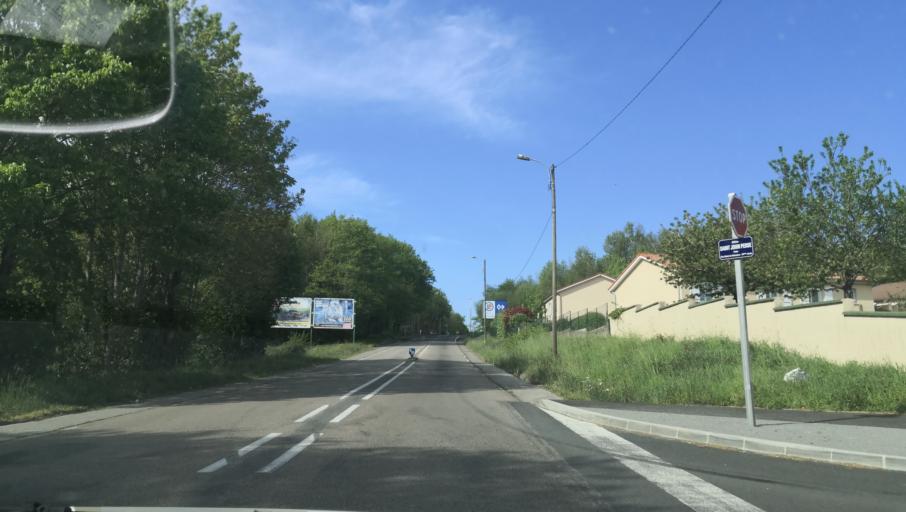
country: FR
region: Limousin
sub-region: Departement de la Haute-Vienne
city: Couzeix
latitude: 45.8648
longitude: 1.2590
